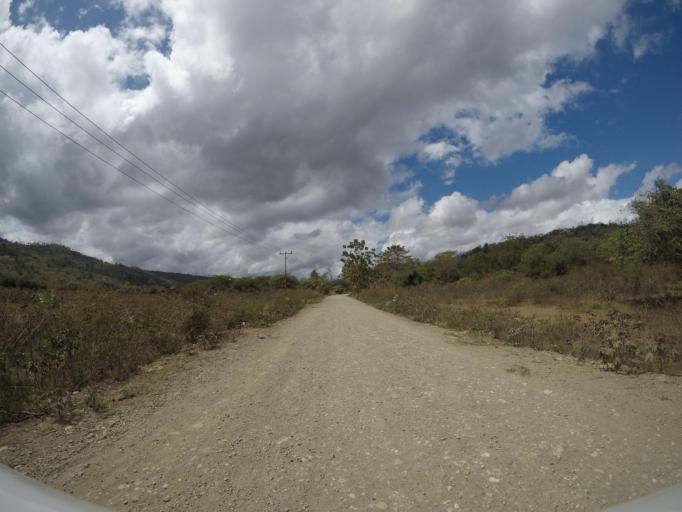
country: TL
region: Lautem
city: Lospalos
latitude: -8.4920
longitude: 126.8229
